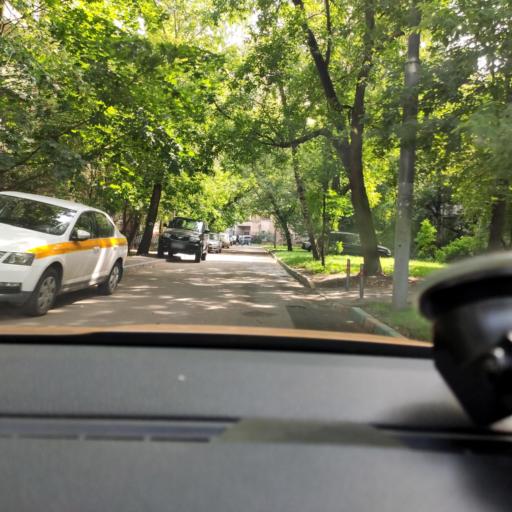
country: RU
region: Moskovskaya
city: Khoroshevo-Mnevniki
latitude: 55.7793
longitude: 37.4904
